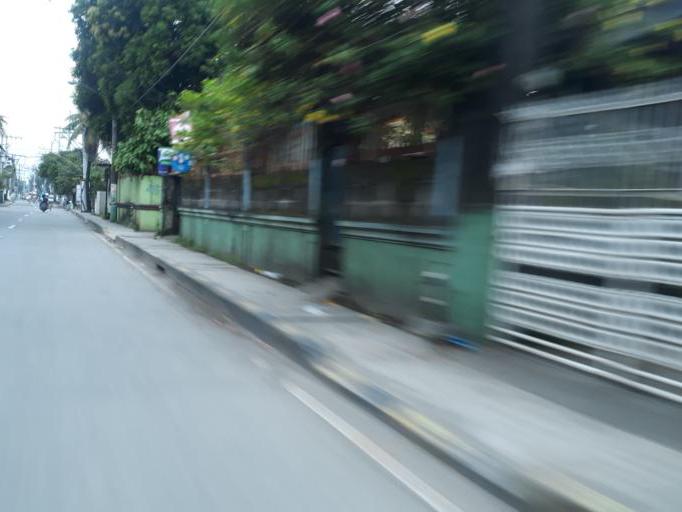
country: PH
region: Calabarzon
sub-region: Province of Rizal
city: Valenzuela
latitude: 14.7075
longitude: 120.9529
